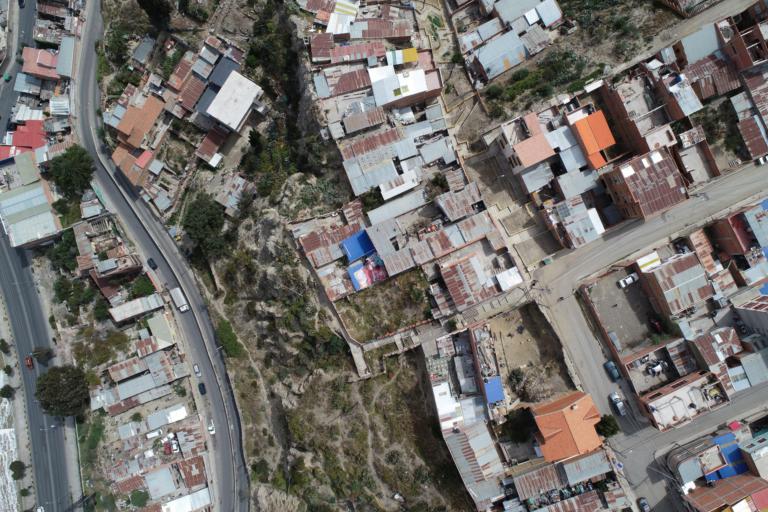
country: BO
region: La Paz
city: La Paz
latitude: -16.5346
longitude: -68.0953
